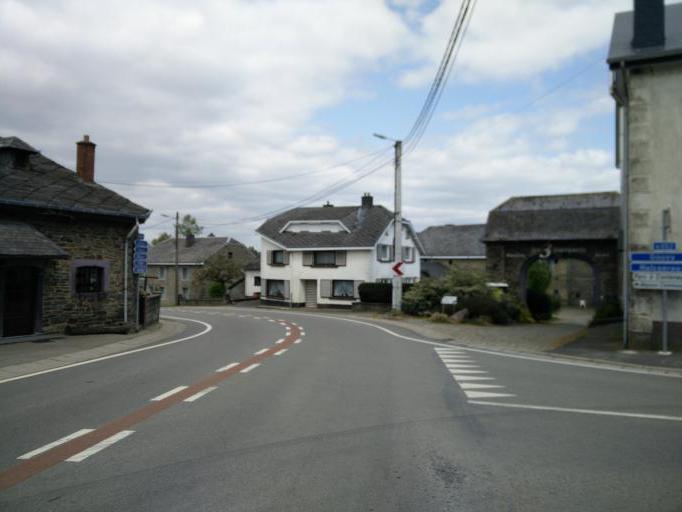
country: BE
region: Wallonia
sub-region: Province du Luxembourg
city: Gouvy
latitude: 50.2142
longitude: 5.9127
